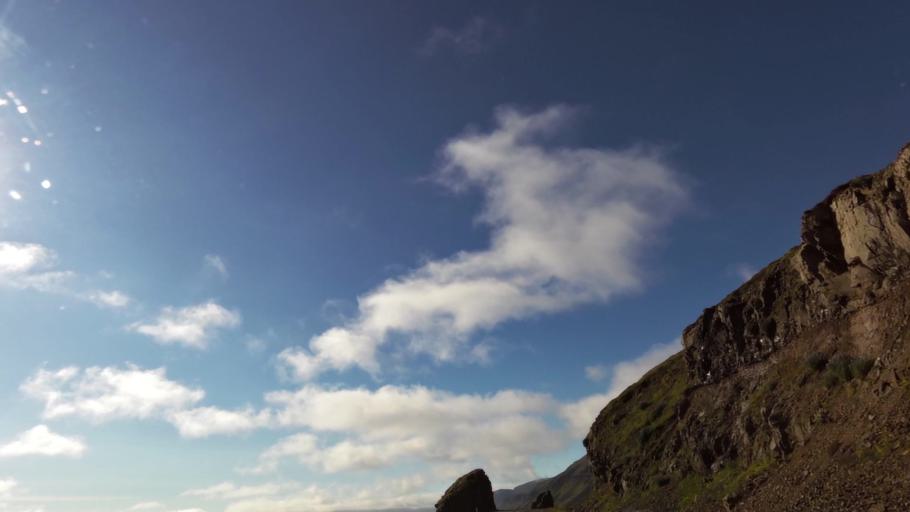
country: IS
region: West
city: Olafsvik
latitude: 65.5448
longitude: -23.8845
